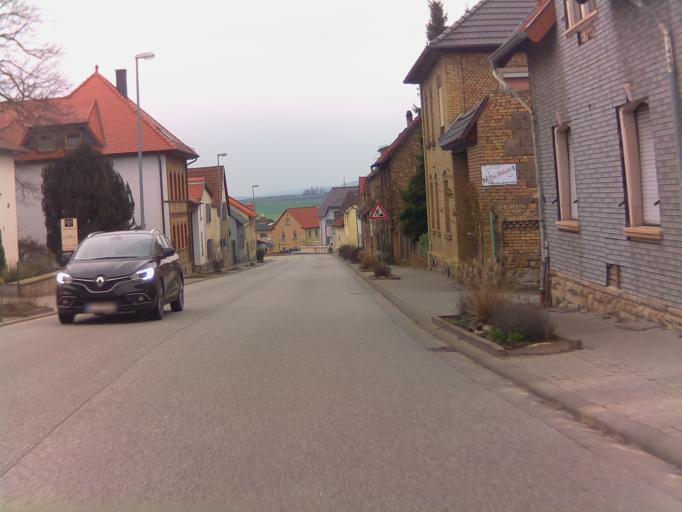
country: DE
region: Rheinland-Pfalz
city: Sulzheim
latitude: 49.8407
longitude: 8.0961
